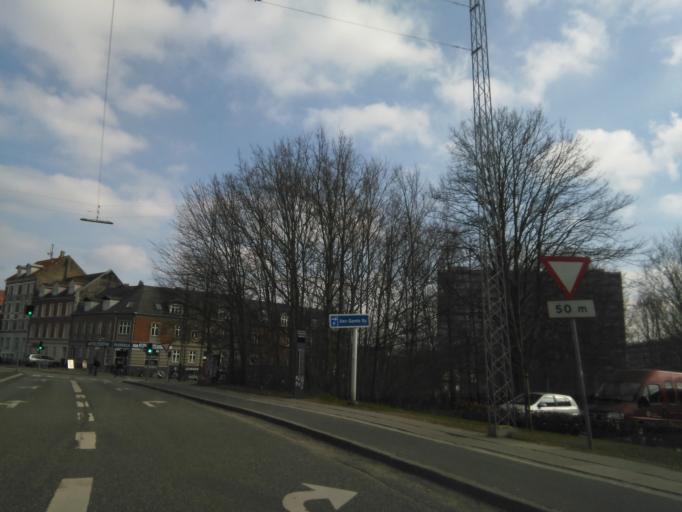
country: DK
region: Central Jutland
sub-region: Arhus Kommune
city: Arhus
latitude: 56.1647
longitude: 10.1964
